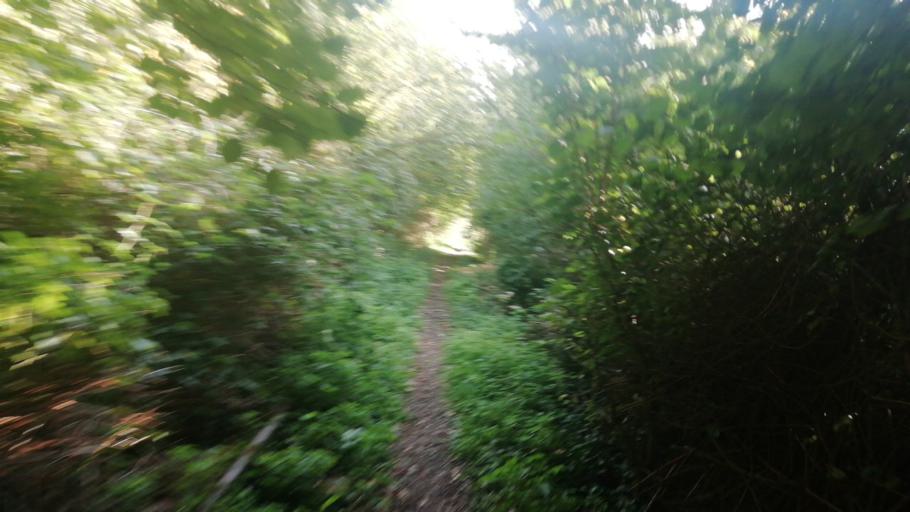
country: FR
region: Haute-Normandie
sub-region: Departement de la Seine-Maritime
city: Rolleville
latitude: 49.5857
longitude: 0.2145
